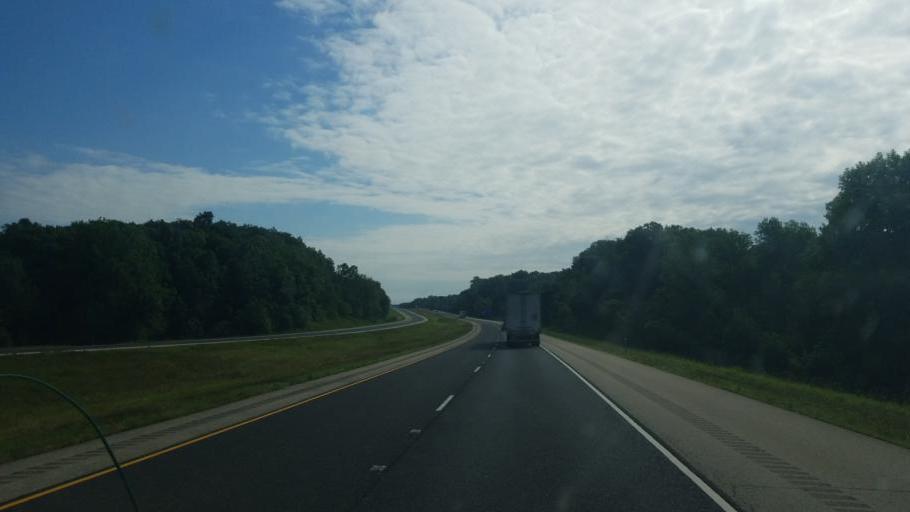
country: US
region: Illinois
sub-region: Clark County
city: Marshall
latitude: 39.4047
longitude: -87.7352
